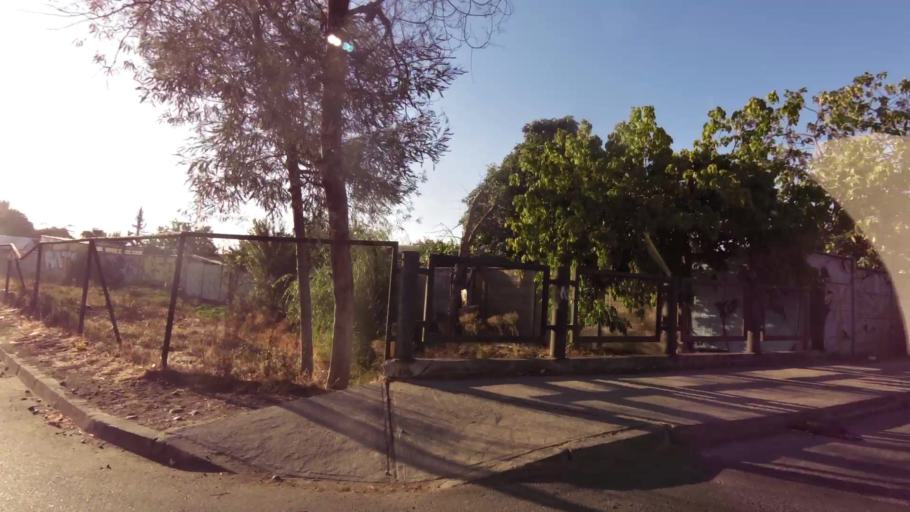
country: CL
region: Maule
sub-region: Provincia de Talca
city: Talca
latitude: -35.4500
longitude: -71.6667
